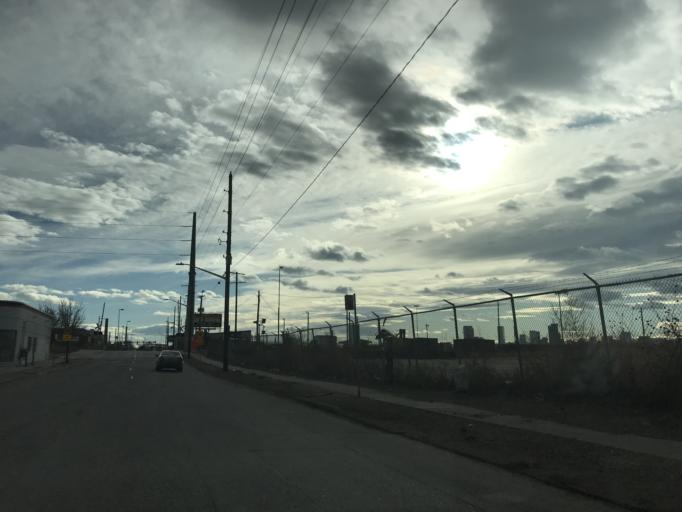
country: US
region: Colorado
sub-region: Adams County
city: Commerce City
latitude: 39.7764
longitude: -104.9594
